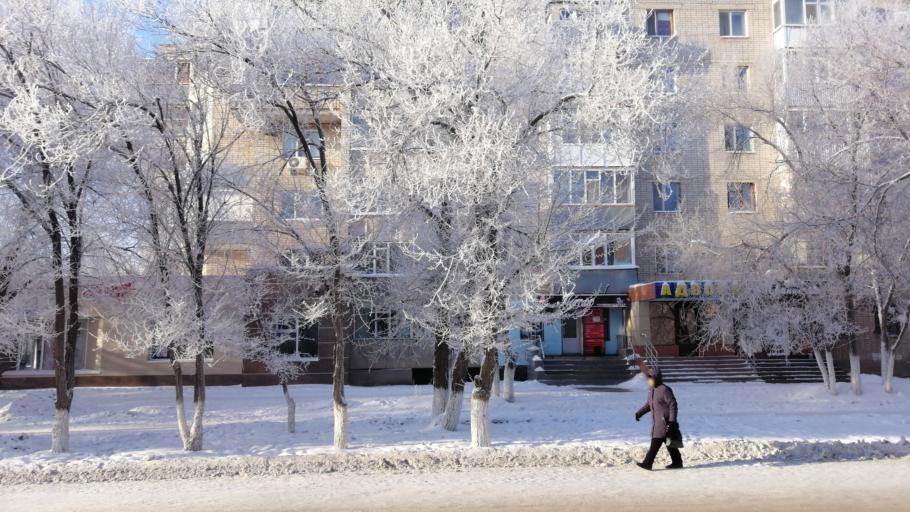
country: KZ
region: Aqtoebe
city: Aqtobe
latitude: 50.2925
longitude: 57.1495
